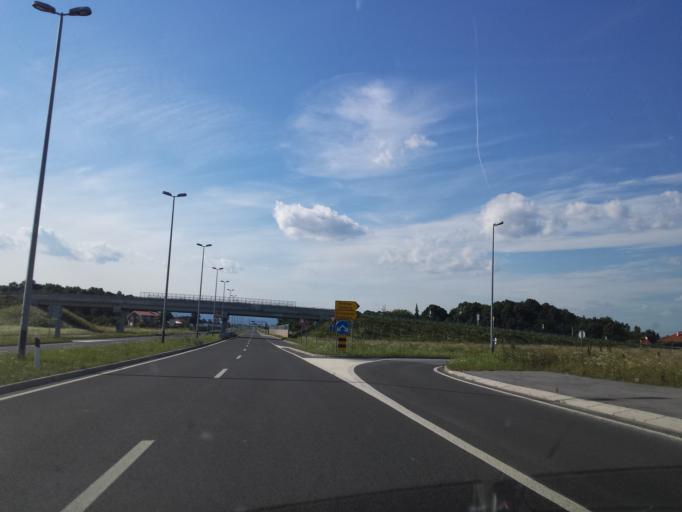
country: HR
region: Zagrebacka
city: Micevec
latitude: 45.7488
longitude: 16.1060
